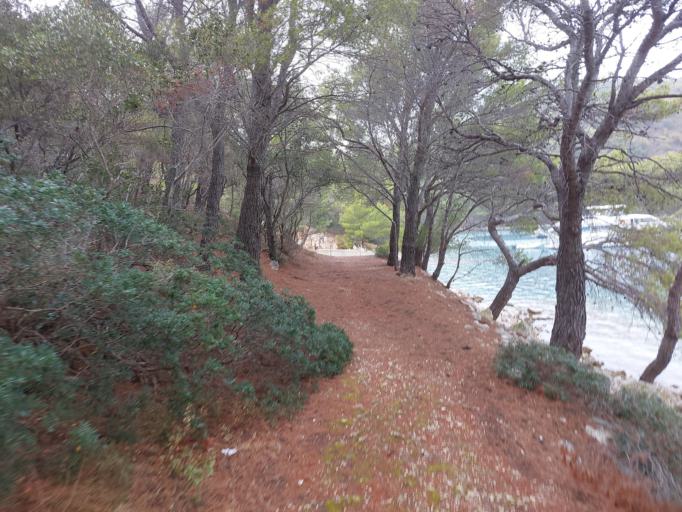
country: HR
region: Dubrovacko-Neretvanska
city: Smokvica
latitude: 42.7565
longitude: 16.8104
